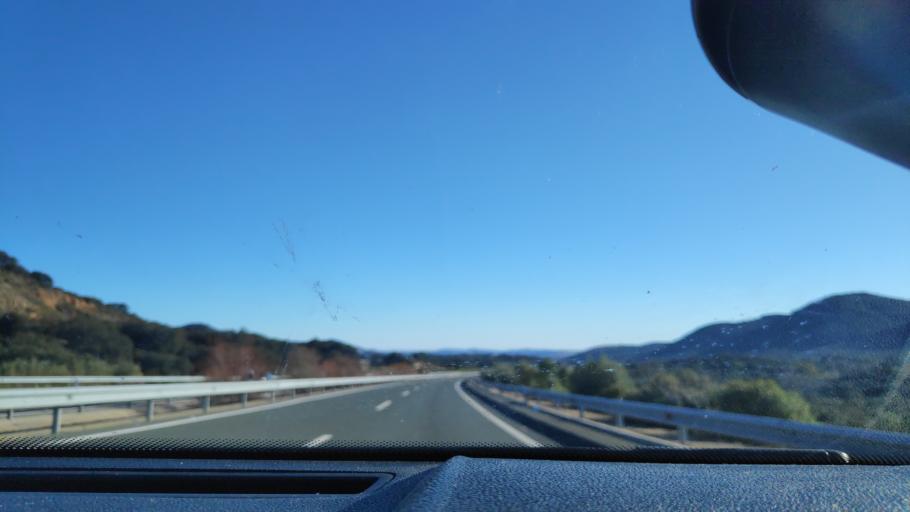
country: ES
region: Extremadura
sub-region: Provincia de Badajoz
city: Monesterio
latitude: 38.0671
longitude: -6.2453
